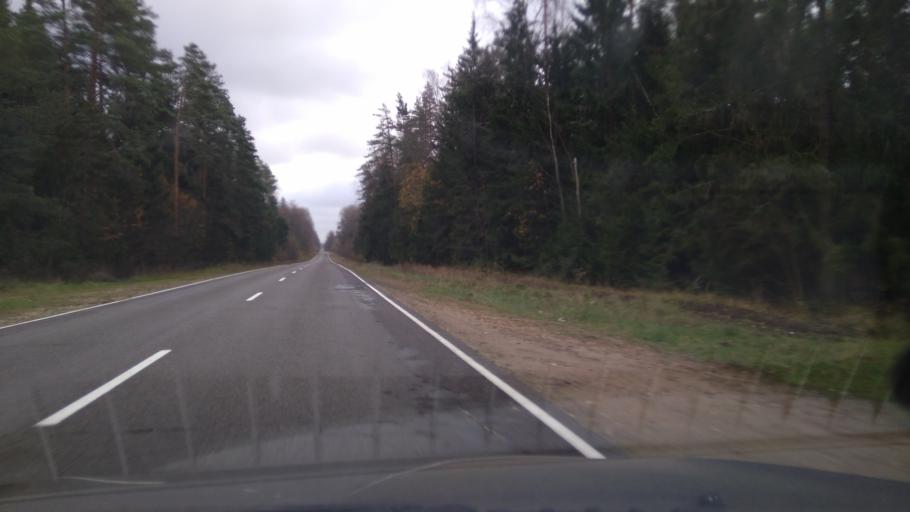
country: BY
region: Minsk
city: Urechcha
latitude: 53.2125
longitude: 27.8788
